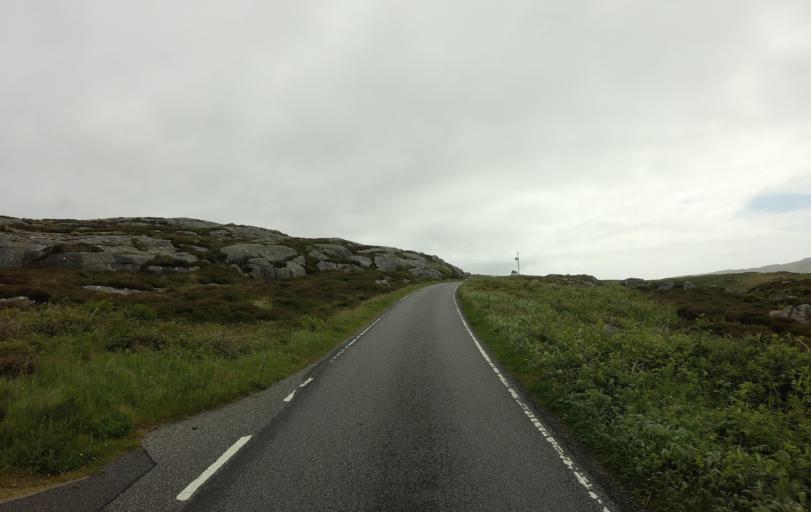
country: GB
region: Scotland
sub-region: Eilean Siar
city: Isle of South Uist
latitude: 57.1059
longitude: -7.3232
